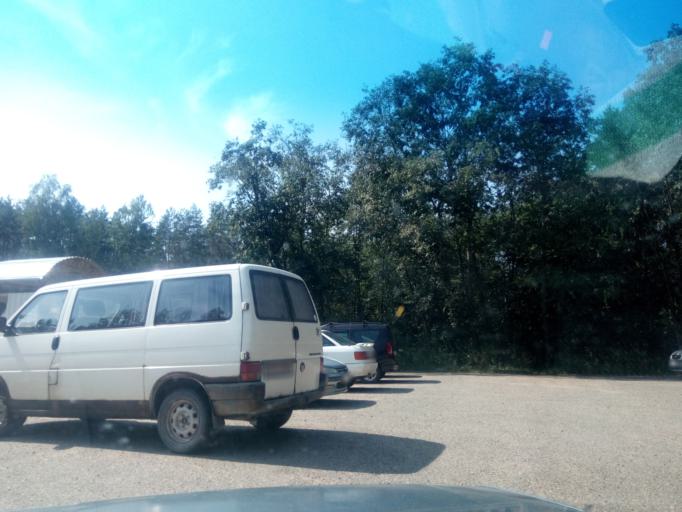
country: BY
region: Vitebsk
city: Vyerkhnyadzvinsk
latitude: 55.7983
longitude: 27.9550
